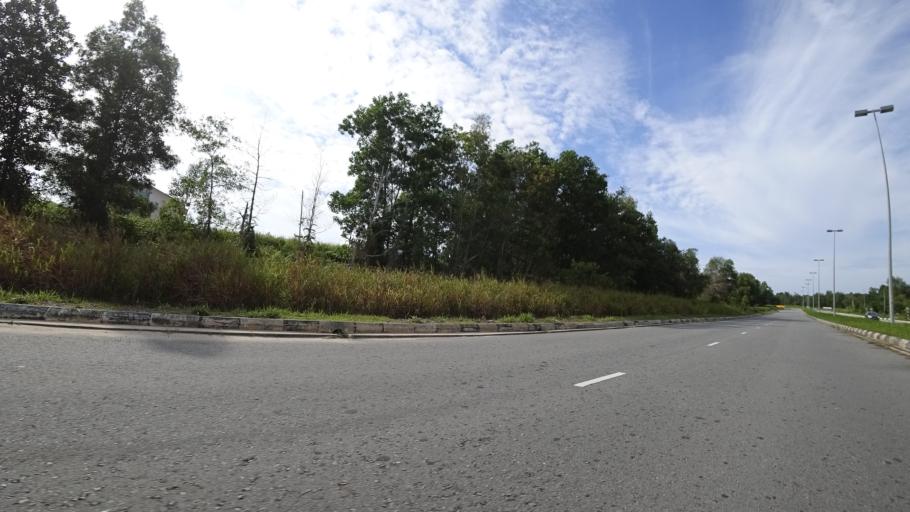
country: BN
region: Brunei and Muara
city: Bandar Seri Begawan
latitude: 4.8945
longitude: 114.8034
